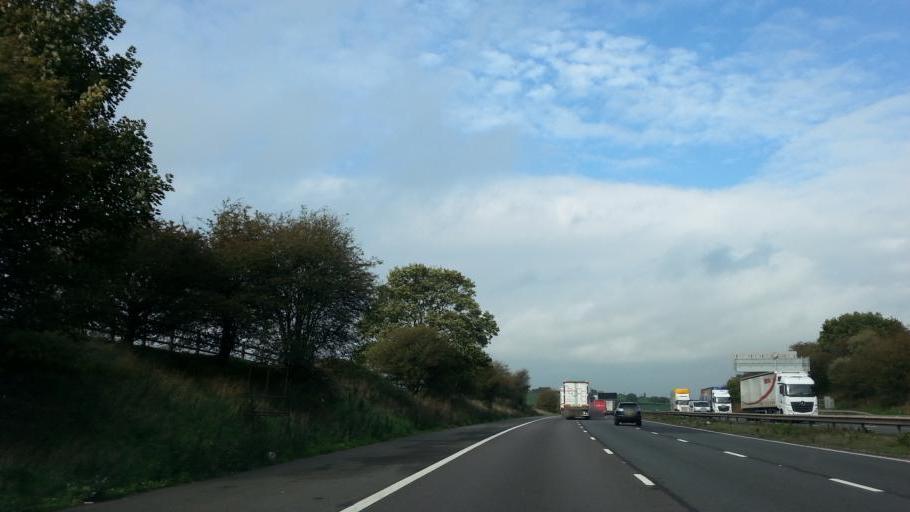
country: GB
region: England
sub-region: Staffordshire
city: Audley
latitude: 53.0308
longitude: -2.3274
